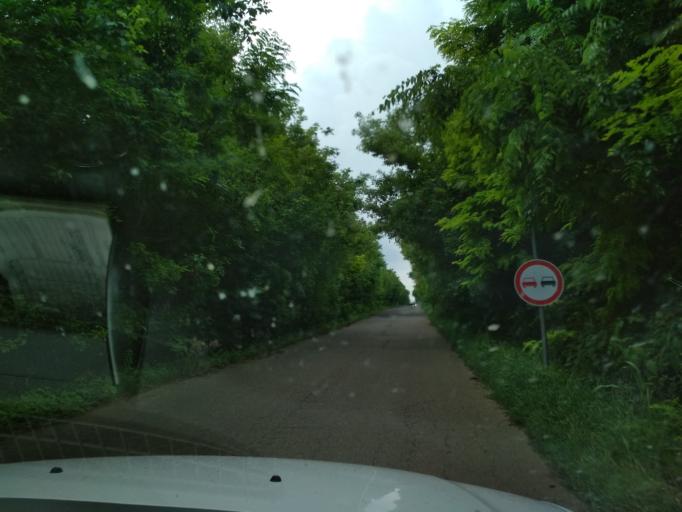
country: HU
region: Pest
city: Cegledbercel
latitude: 47.2795
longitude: 19.6841
